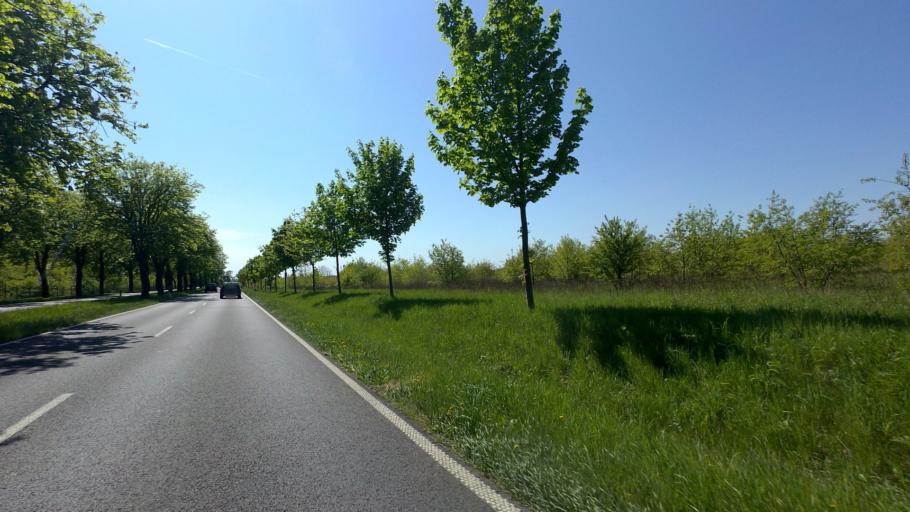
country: DE
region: Brandenburg
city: Konigs Wusterhausen
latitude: 52.3061
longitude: 13.6025
